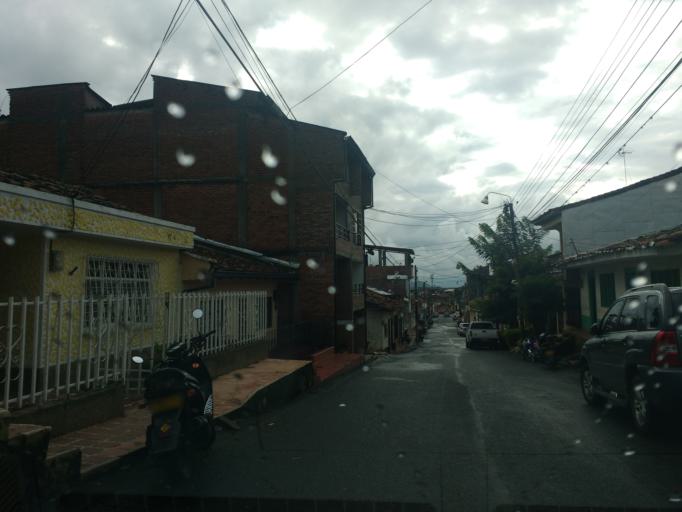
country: CO
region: Cauca
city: Santander de Quilichao
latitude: 3.0019
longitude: -76.4795
